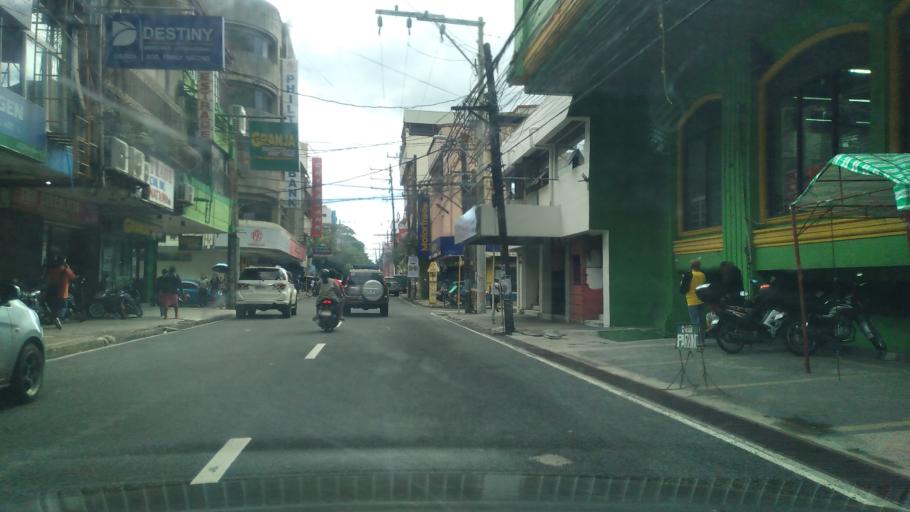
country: PH
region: Calabarzon
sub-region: Province of Quezon
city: Lucena
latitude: 13.9322
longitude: 121.6127
